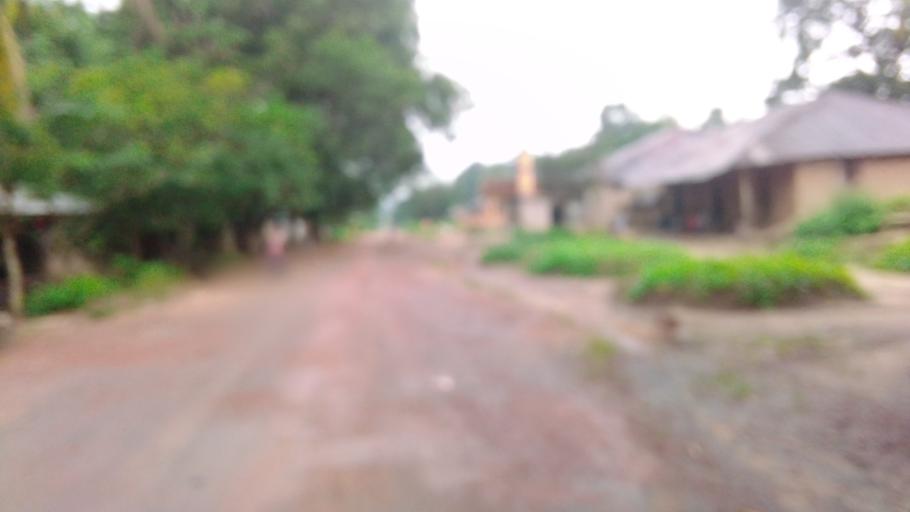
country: SL
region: Northern Province
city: Lunsar
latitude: 8.6897
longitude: -12.5207
